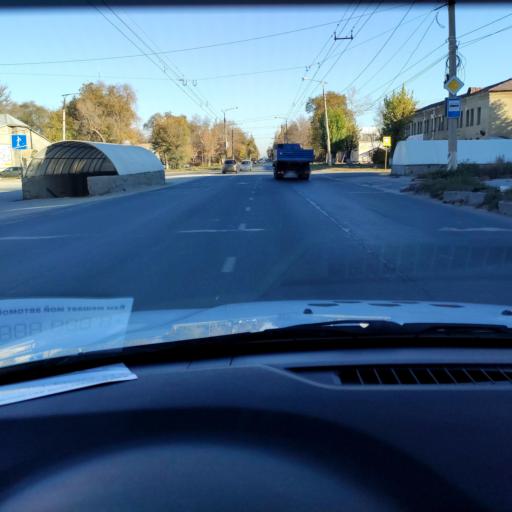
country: RU
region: Samara
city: Tol'yatti
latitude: 53.5626
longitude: 49.4551
